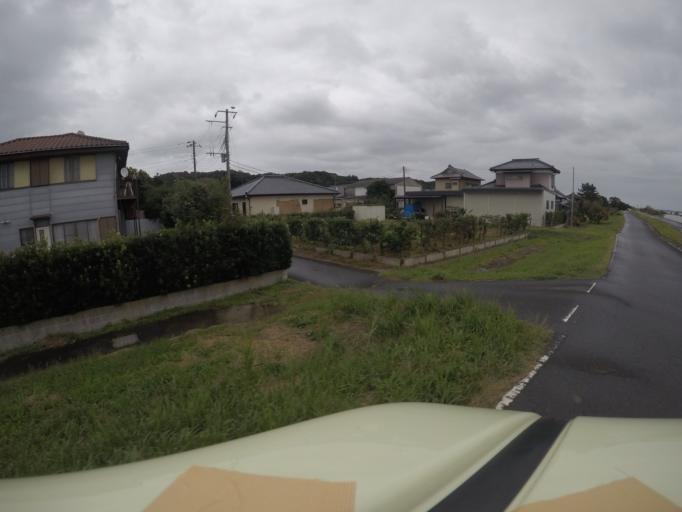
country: JP
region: Ibaraki
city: Itako
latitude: 36.0066
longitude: 140.4683
